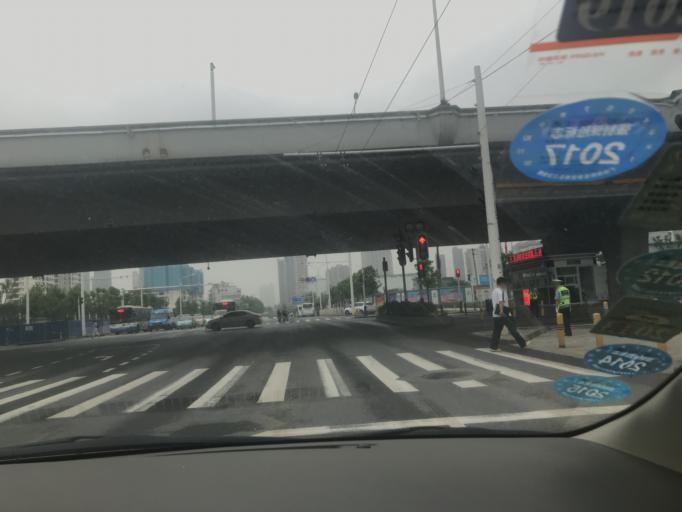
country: CN
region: Hubei
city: Yongfeng
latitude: 30.5560
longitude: 114.2366
